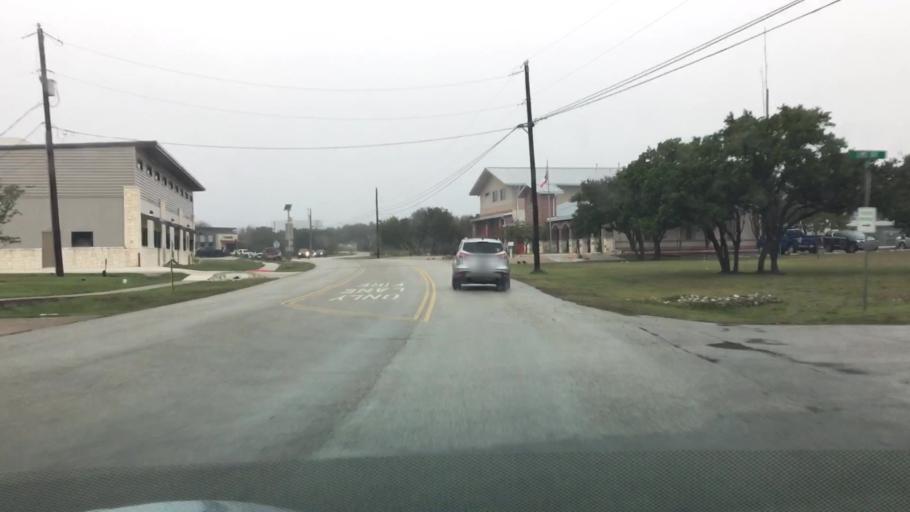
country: US
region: Texas
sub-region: Hays County
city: Dripping Springs
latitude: 30.1954
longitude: -98.0965
